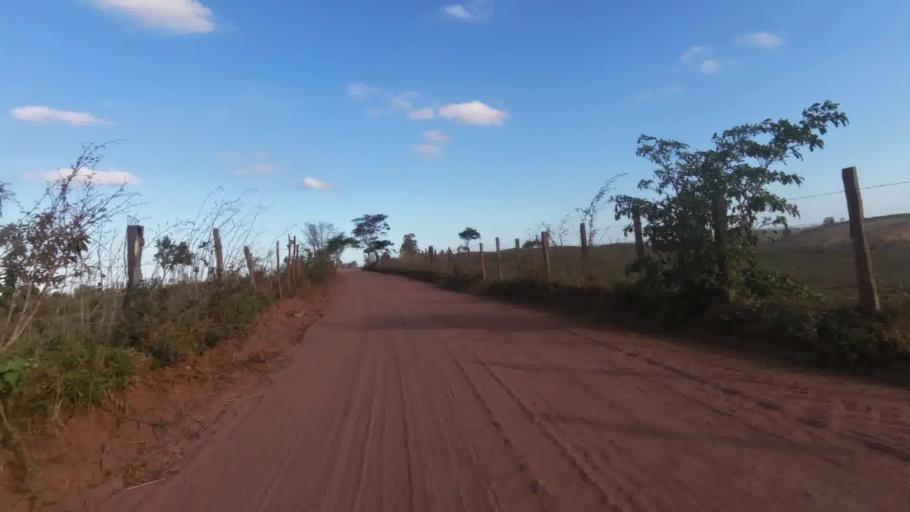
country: BR
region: Espirito Santo
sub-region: Marataizes
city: Marataizes
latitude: -21.1594
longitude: -41.0586
